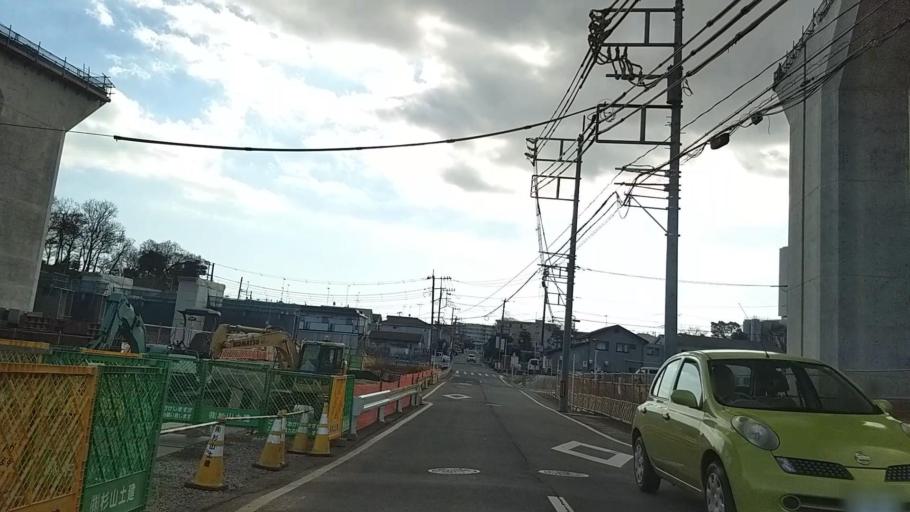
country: JP
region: Kanagawa
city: Isehara
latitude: 35.4097
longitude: 139.3184
